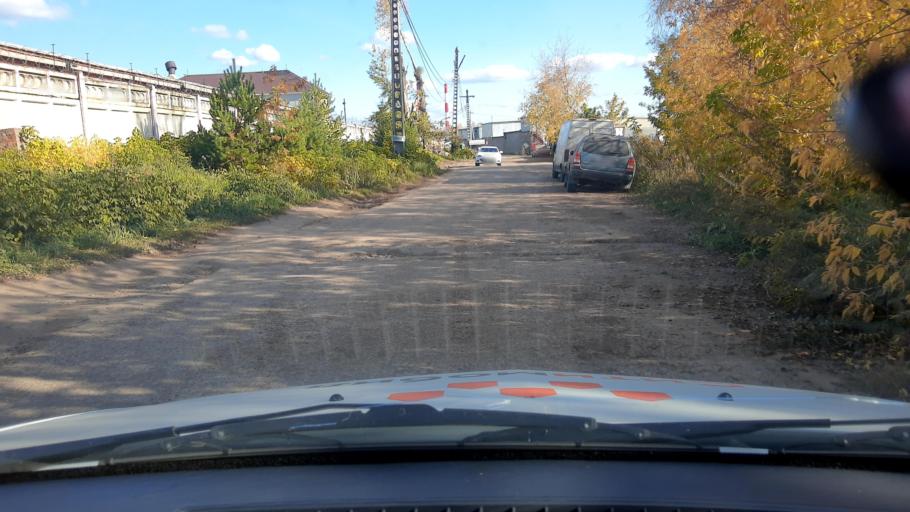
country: RU
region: Bashkortostan
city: Ufa
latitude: 54.7958
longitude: 56.0908
